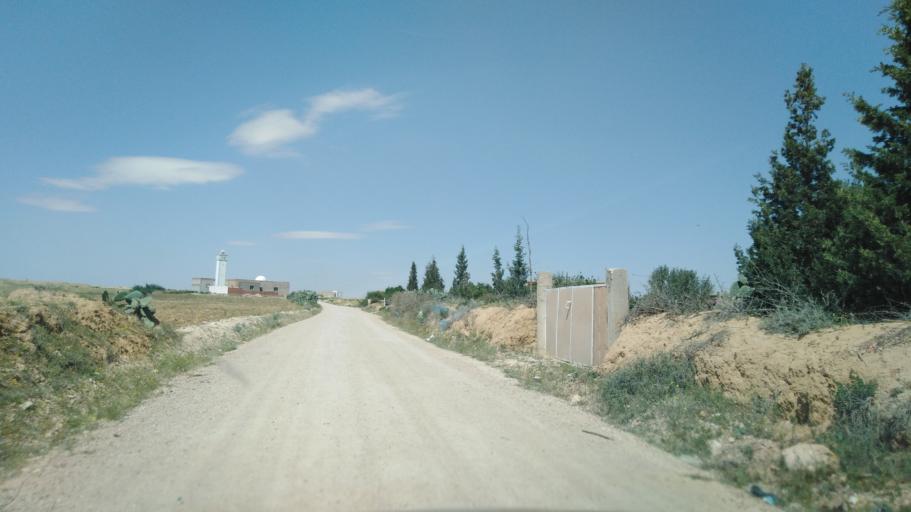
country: TN
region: Safaqis
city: Sfax
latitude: 34.7590
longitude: 10.5283
